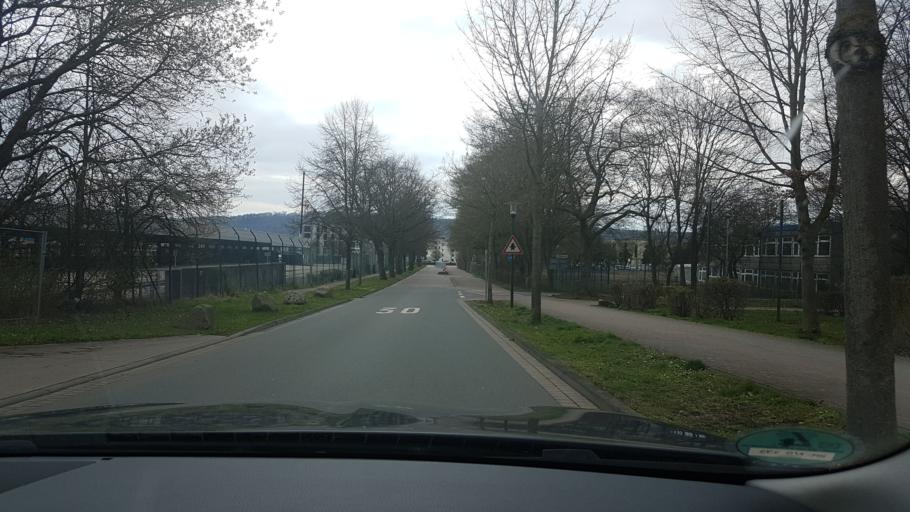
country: DE
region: Lower Saxony
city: Hameln
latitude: 52.1245
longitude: 9.3479
